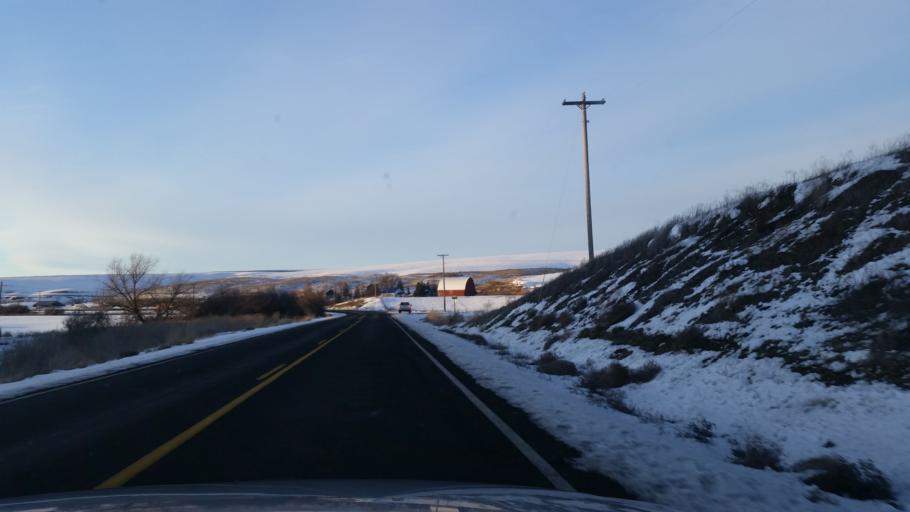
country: US
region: Washington
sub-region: Whitman County
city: Colfax
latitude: 47.1140
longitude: -117.6406
